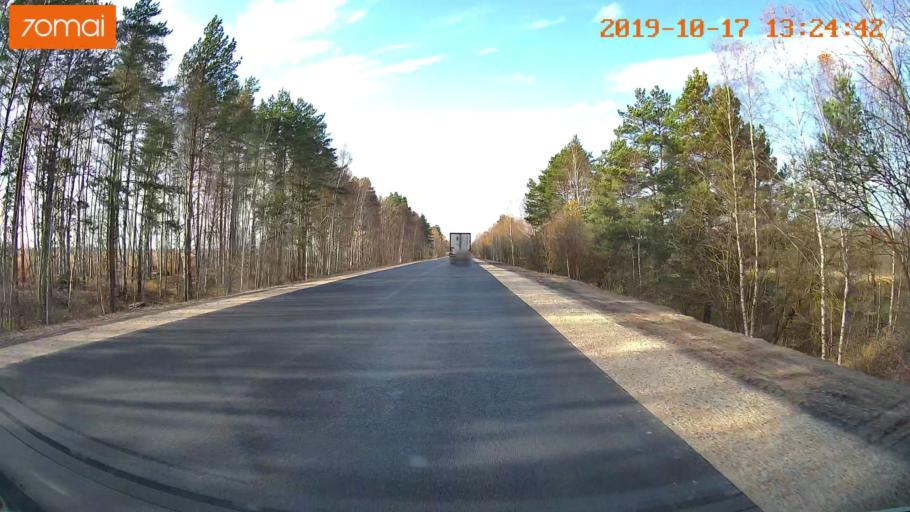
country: RU
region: Rjazan
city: Gus'-Zheleznyy
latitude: 55.0971
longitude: 40.9584
